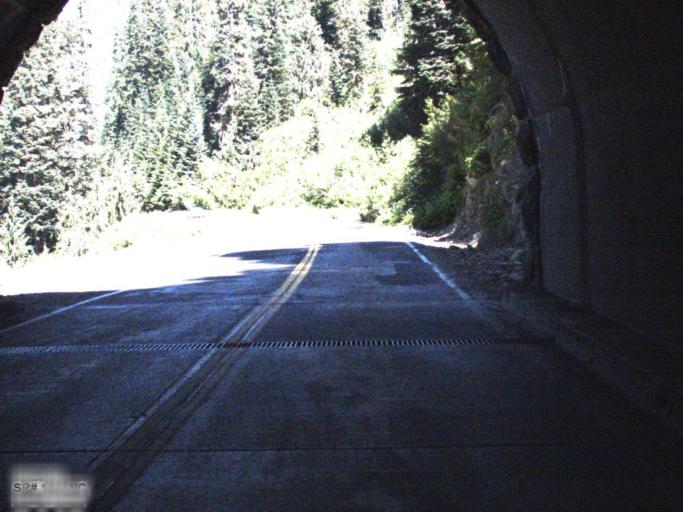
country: US
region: Washington
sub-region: King County
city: Enumclaw
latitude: 46.8465
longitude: -121.5269
